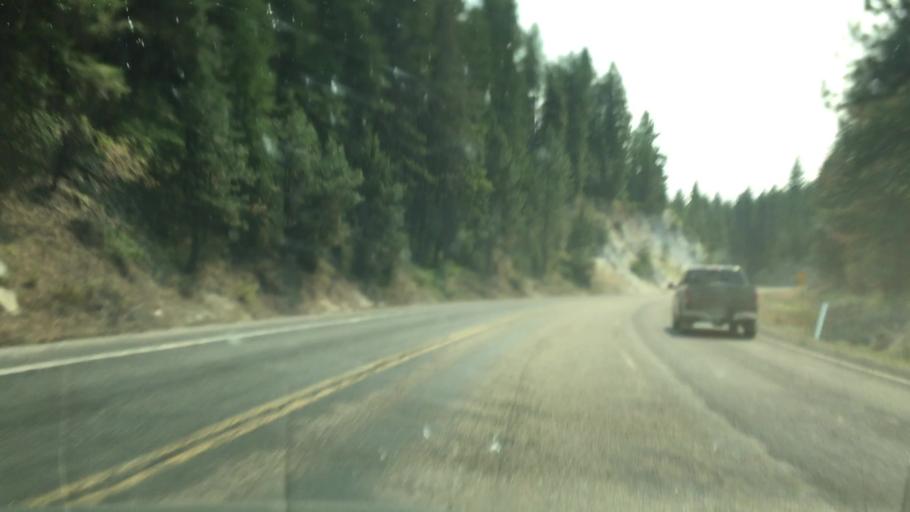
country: US
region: Idaho
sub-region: Valley County
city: Cascade
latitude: 44.5843
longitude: -116.0384
